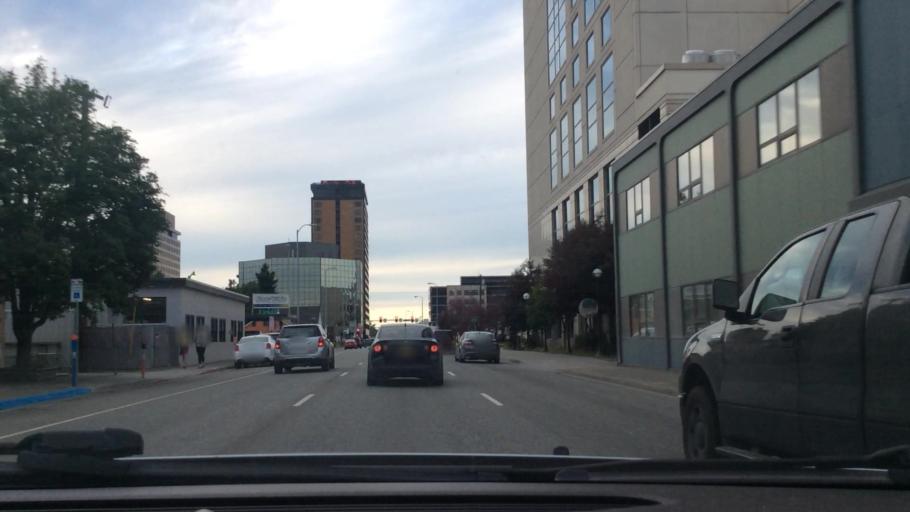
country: US
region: Alaska
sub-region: Anchorage Municipality
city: Anchorage
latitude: 61.2149
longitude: -149.8995
